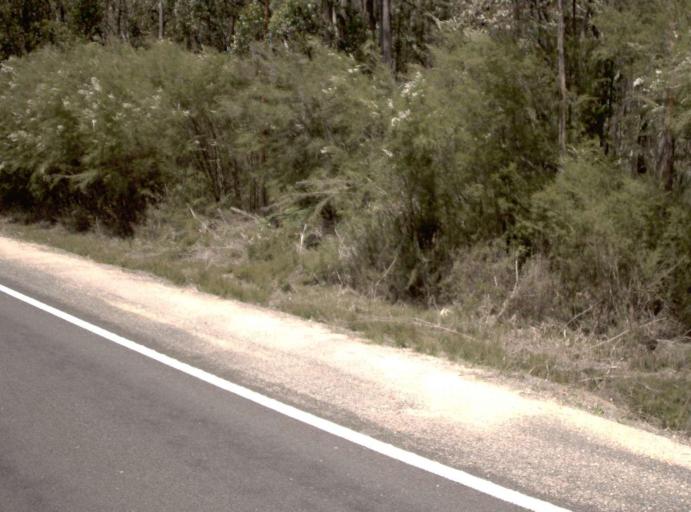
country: AU
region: Victoria
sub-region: East Gippsland
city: Lakes Entrance
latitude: -37.6842
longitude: 148.7672
